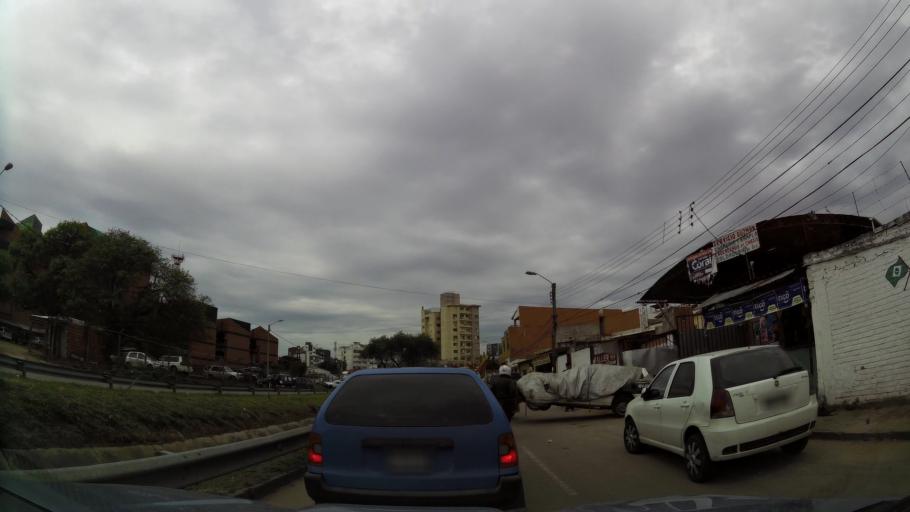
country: BO
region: Santa Cruz
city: Santa Cruz de la Sierra
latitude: -17.7686
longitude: -63.2028
